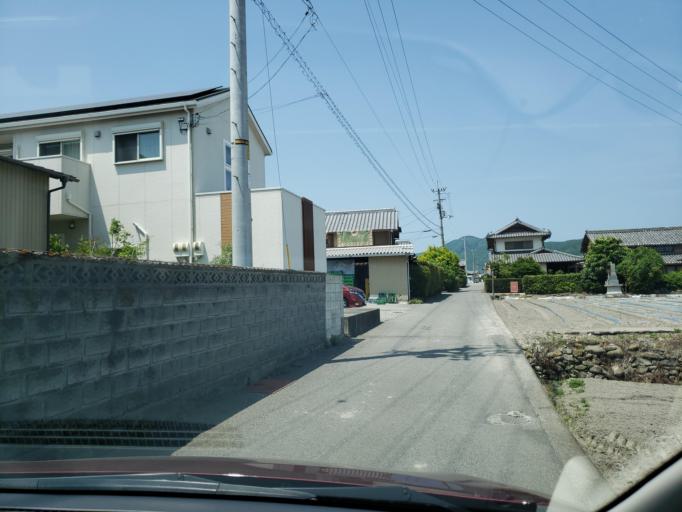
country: JP
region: Tokushima
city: Kamojimacho-jogejima
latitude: 34.0886
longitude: 134.2681
